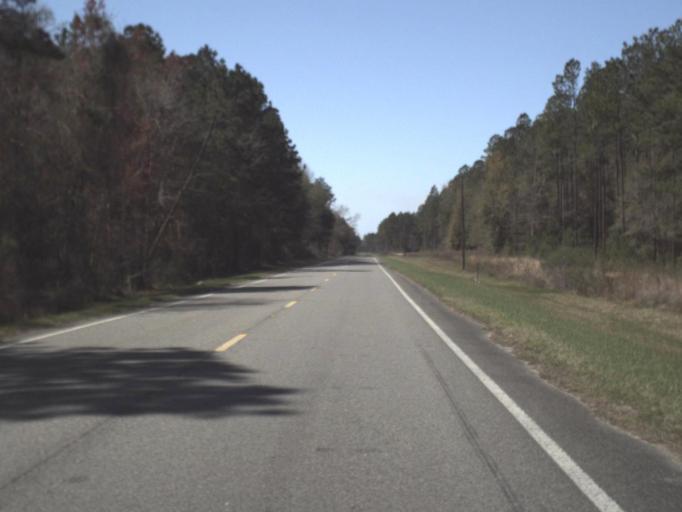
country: US
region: Florida
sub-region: Leon County
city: Woodville
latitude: 30.3411
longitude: -84.0135
